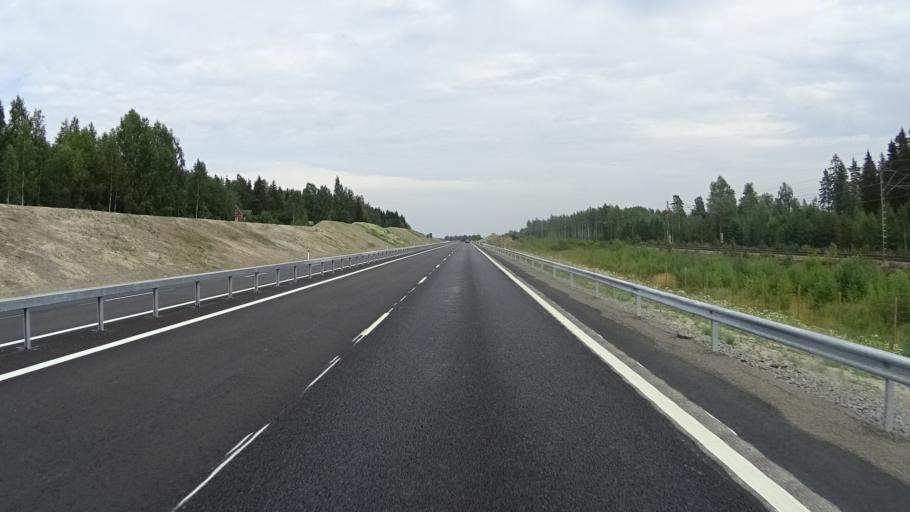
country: FI
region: South Karelia
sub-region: Lappeenranta
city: Lemi
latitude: 60.9398
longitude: 27.7266
